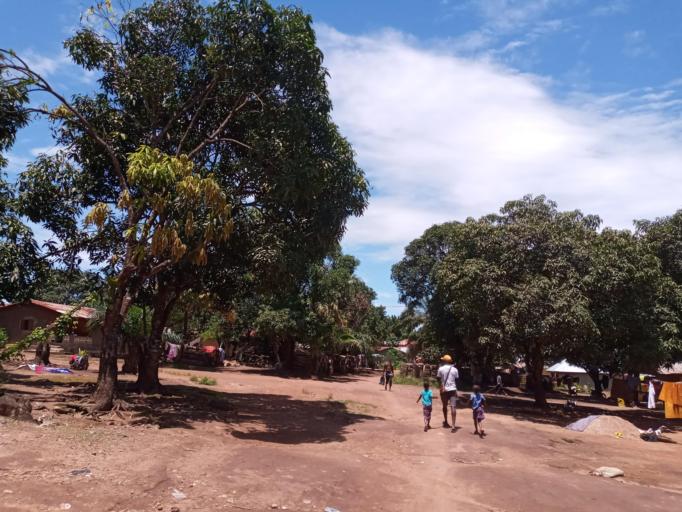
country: SL
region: Eastern Province
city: Koidu
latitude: 8.6384
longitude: -10.9547
